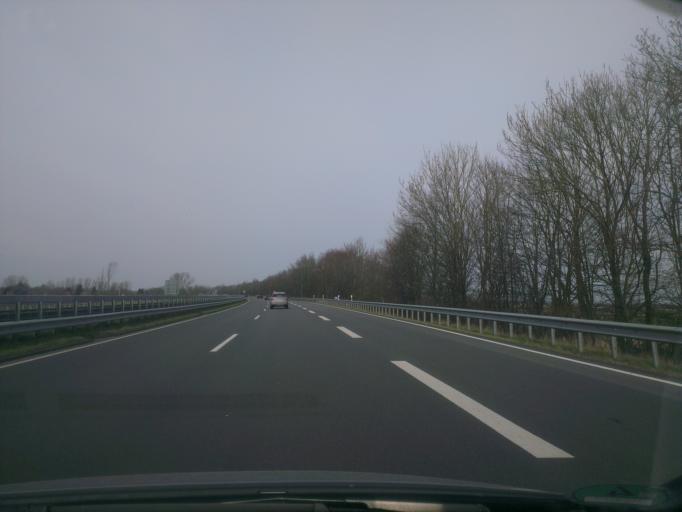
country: DE
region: Lower Saxony
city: Emden
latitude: 53.3793
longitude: 7.2382
